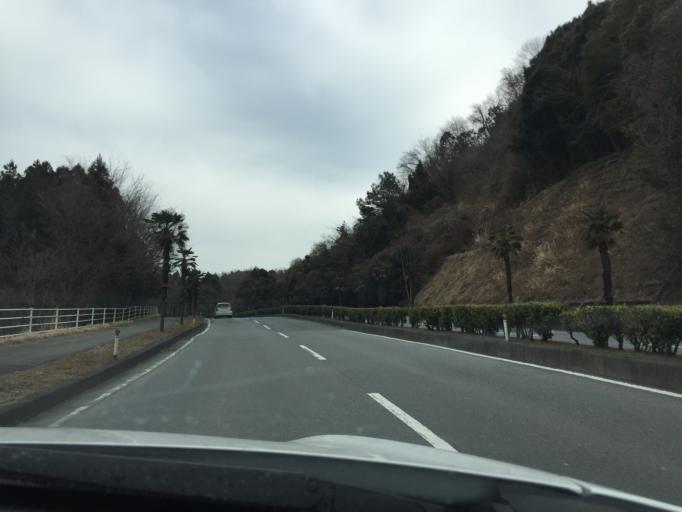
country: JP
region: Fukushima
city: Iwaki
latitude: 36.9886
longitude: 140.8255
